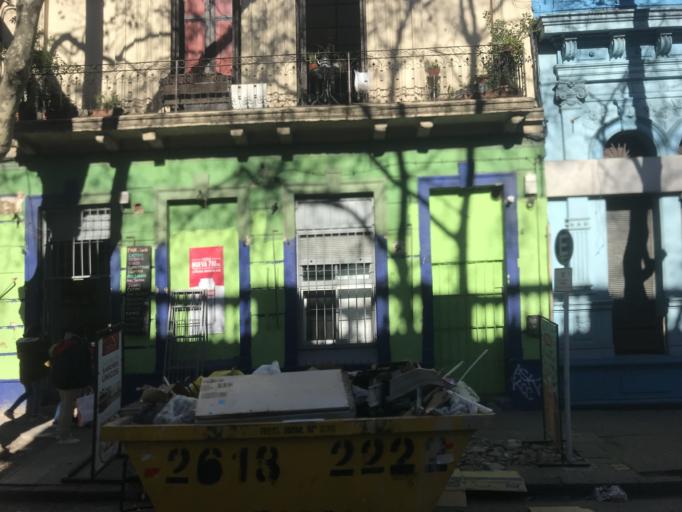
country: UY
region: Montevideo
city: Montevideo
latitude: -34.9023
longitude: -56.1845
